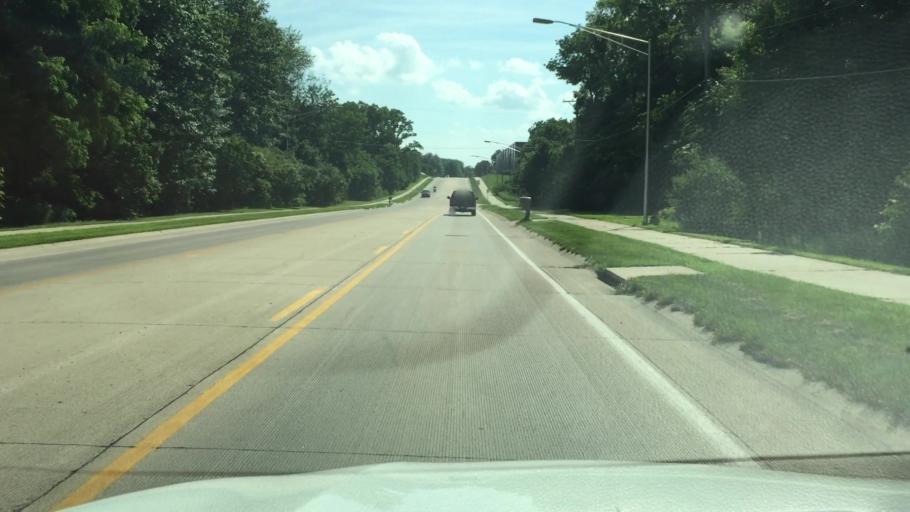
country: US
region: Iowa
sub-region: Johnson County
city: Iowa City
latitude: 41.6795
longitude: -91.5116
